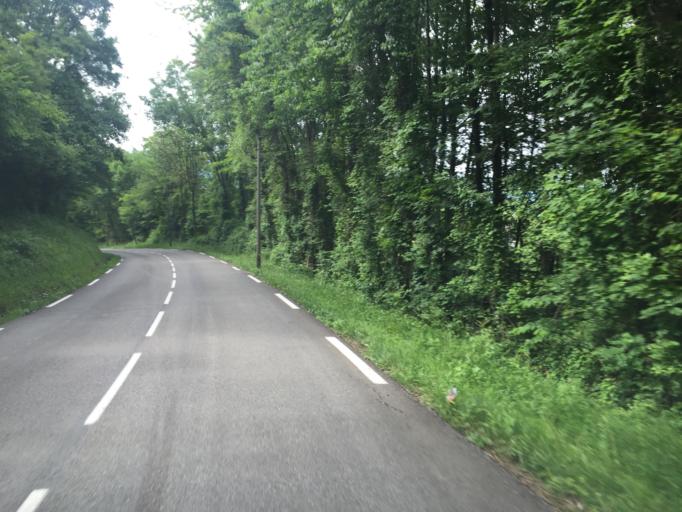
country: FR
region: Rhone-Alpes
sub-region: Departement de la Savoie
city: Jacob-Bellecombette
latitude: 45.5271
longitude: 5.9142
